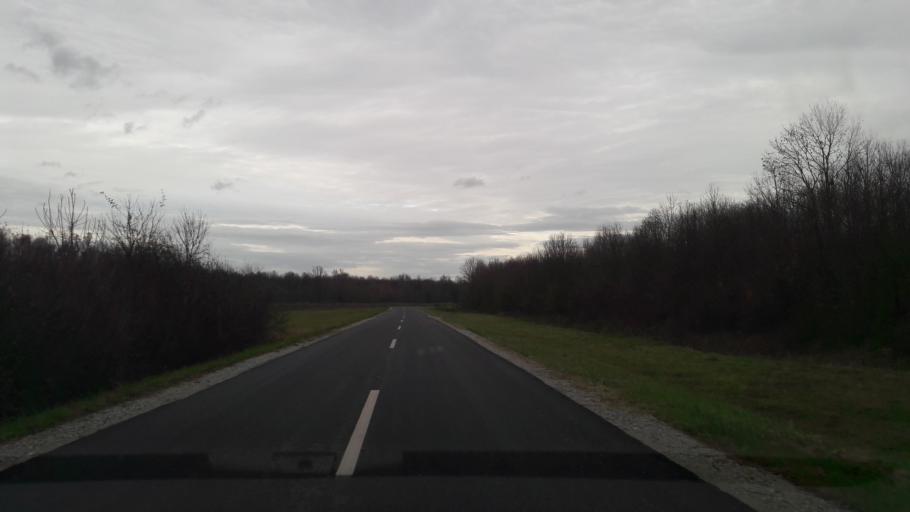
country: HR
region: Osjecko-Baranjska
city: Velimirovac
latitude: 45.6240
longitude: 18.0845
